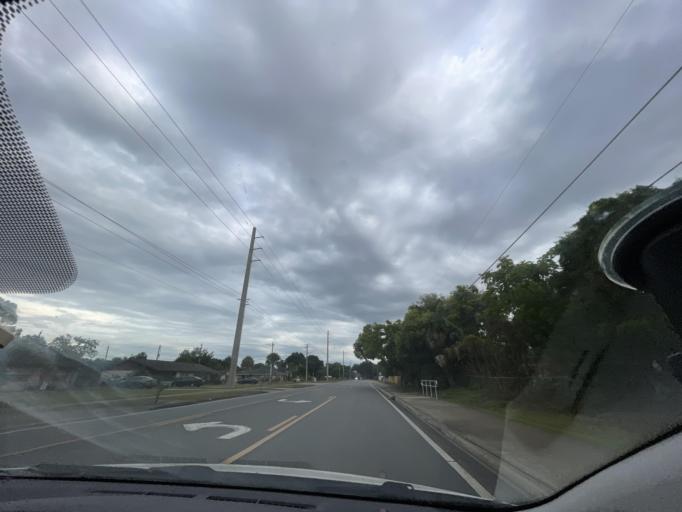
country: US
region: Florida
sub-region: Volusia County
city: Port Orange
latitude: 29.1053
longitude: -80.9933
